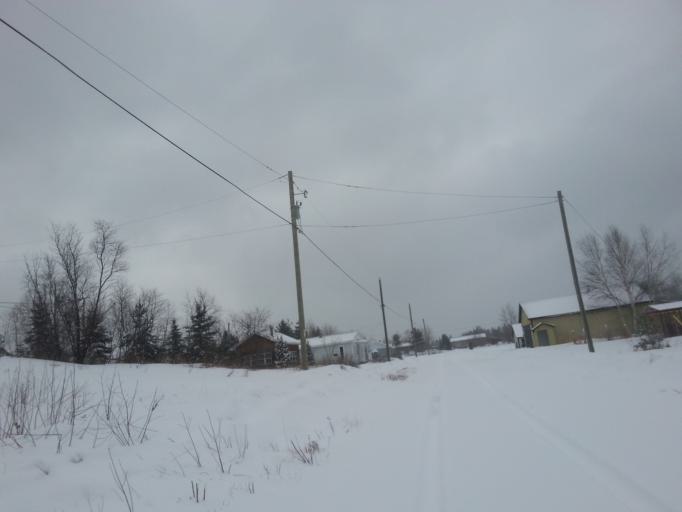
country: CA
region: Ontario
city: Kirkland Lake
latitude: 47.9369
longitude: -80.6509
